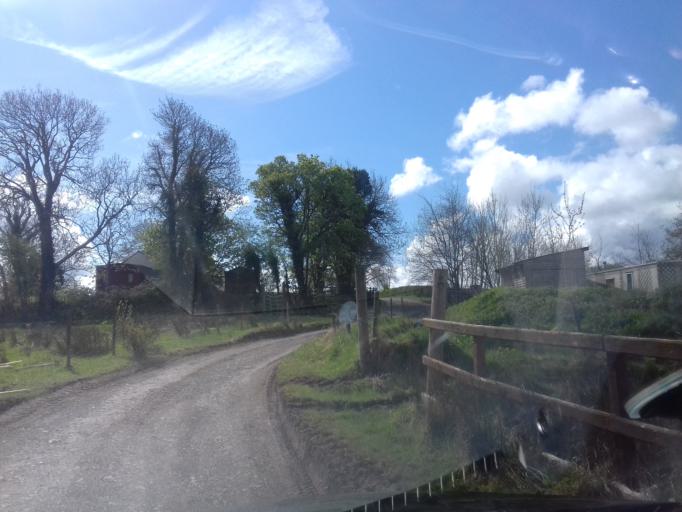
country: GB
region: Northern Ireland
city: Lisnaskea
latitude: 54.1907
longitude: -7.4921
